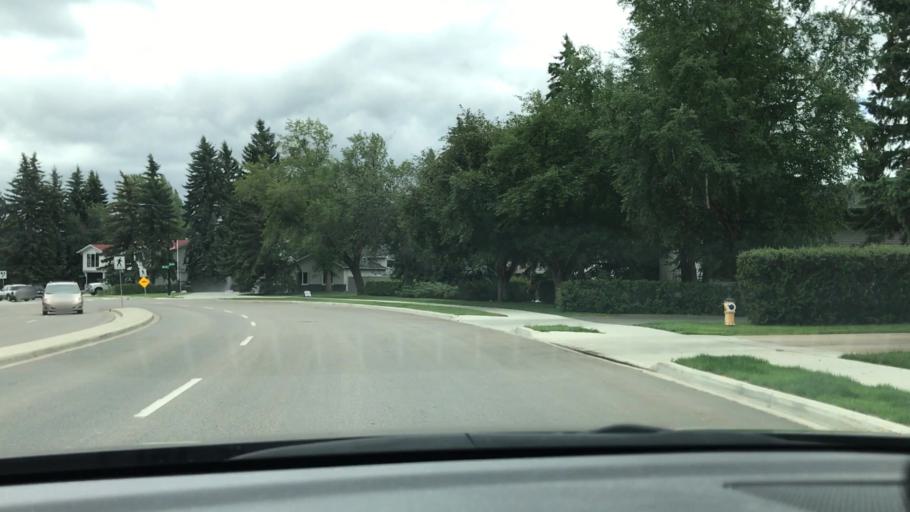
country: CA
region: Alberta
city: Edmonton
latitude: 53.5181
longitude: -113.5597
